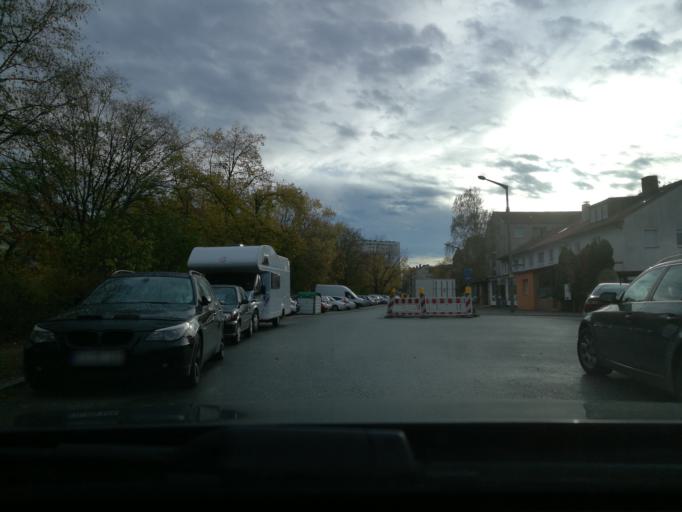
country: DE
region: Bavaria
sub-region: Regierungsbezirk Mittelfranken
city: Furth
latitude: 49.4818
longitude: 10.9513
